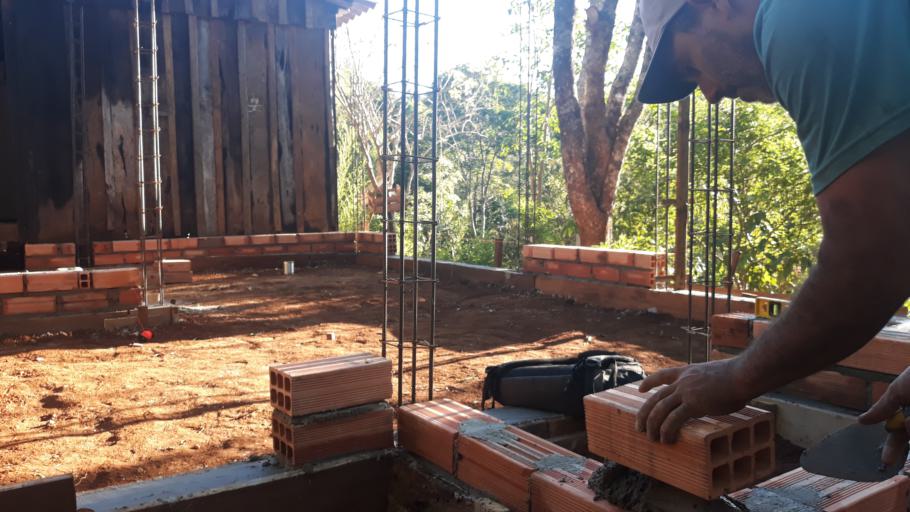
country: AR
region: Misiones
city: Bernardo de Irigoyen
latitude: -26.2708
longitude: -53.6680
